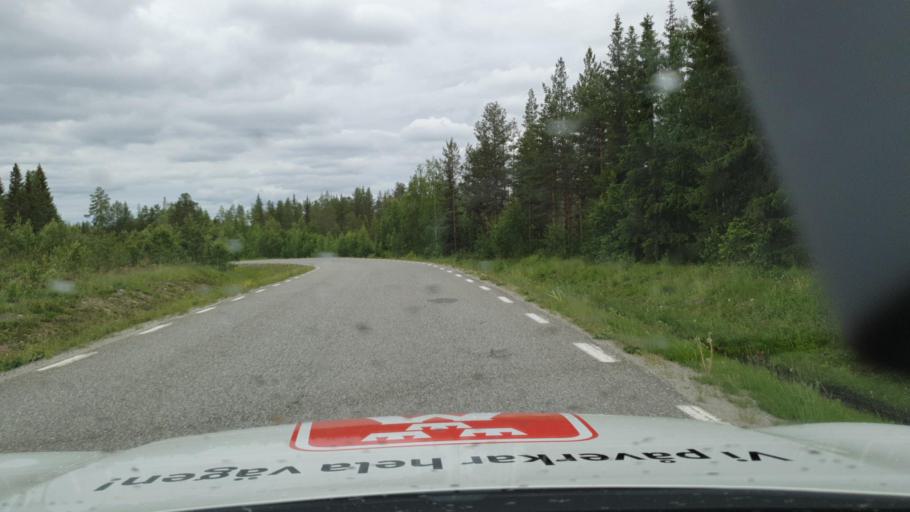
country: SE
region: Vaesterbotten
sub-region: Lycksele Kommun
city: Lycksele
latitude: 64.2463
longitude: 18.2193
